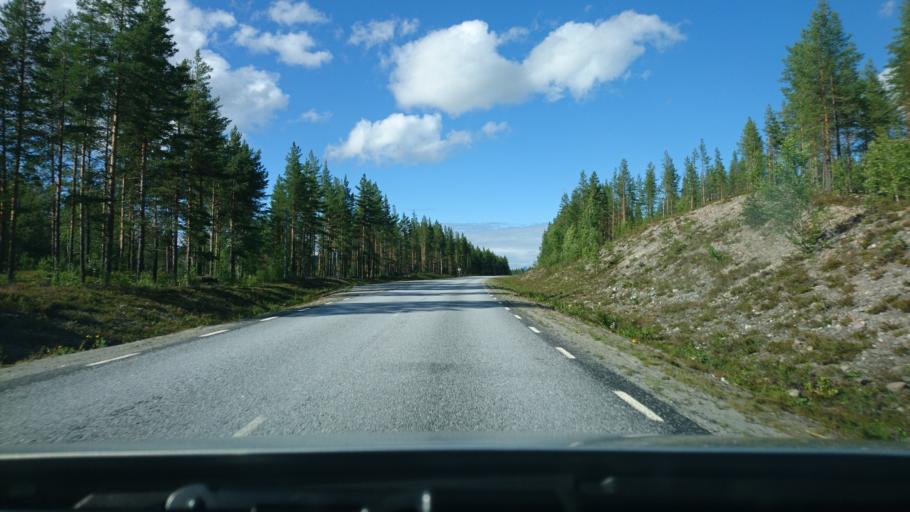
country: SE
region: Vaesterbotten
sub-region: Asele Kommun
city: Asele
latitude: 64.2948
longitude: 17.2584
